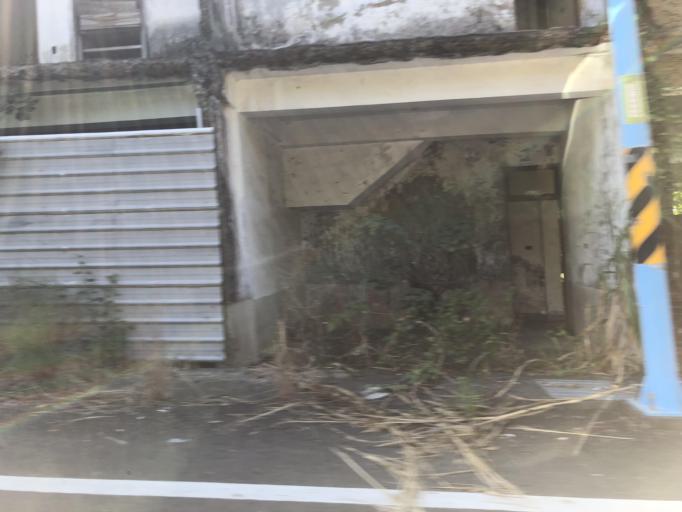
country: TW
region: Taiwan
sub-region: Tainan
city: Tainan
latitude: 23.0370
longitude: 120.3402
